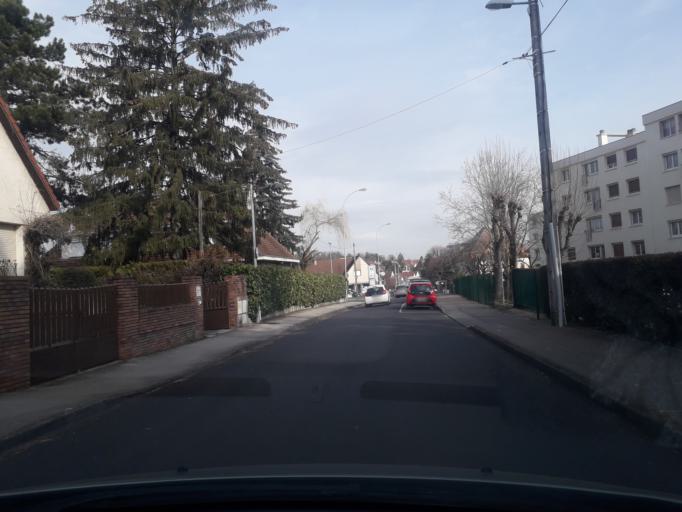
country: FR
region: Bourgogne
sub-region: Departement de la Cote-d'Or
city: Fontaine-les-Dijon
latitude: 47.3367
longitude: 5.0162
